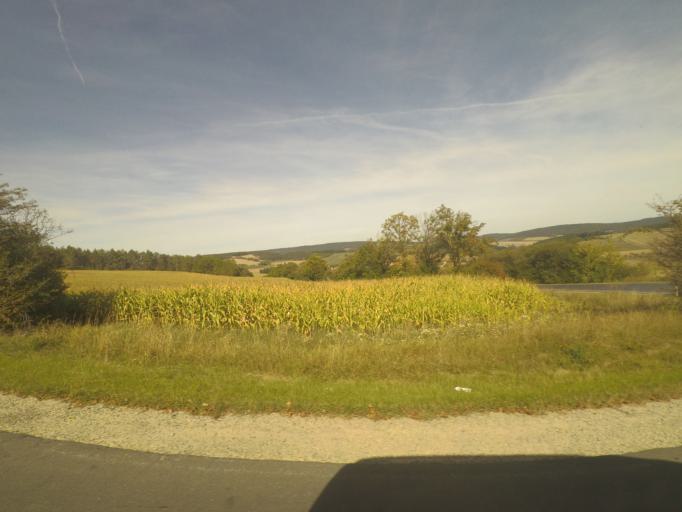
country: DE
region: Thuringia
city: Rottenbach
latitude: 50.7402
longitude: 11.2175
